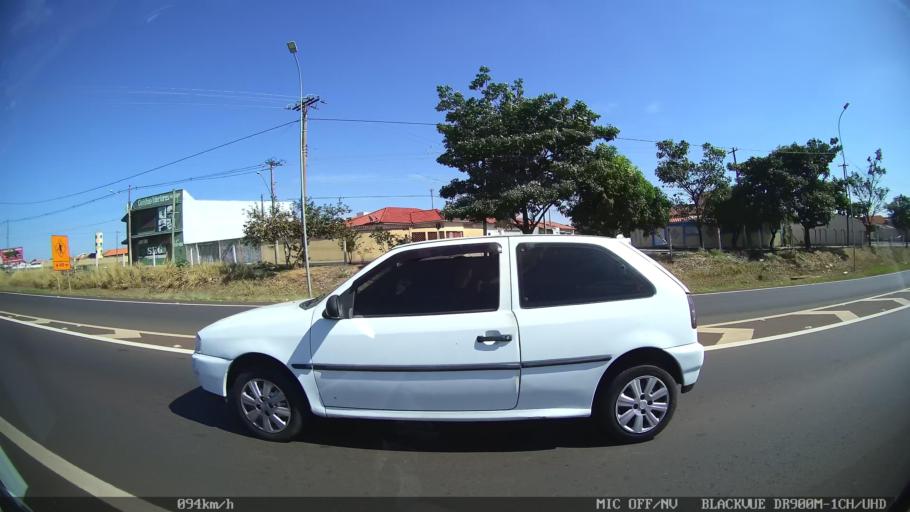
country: BR
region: Sao Paulo
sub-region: Franca
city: Franca
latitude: -20.4921
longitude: -47.4077
